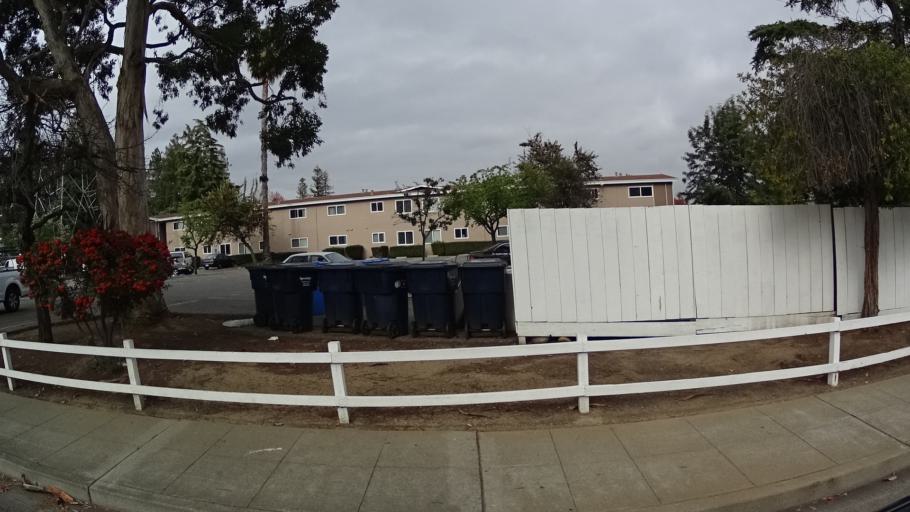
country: US
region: California
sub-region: Santa Clara County
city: Sunnyvale
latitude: 37.3667
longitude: -122.0408
